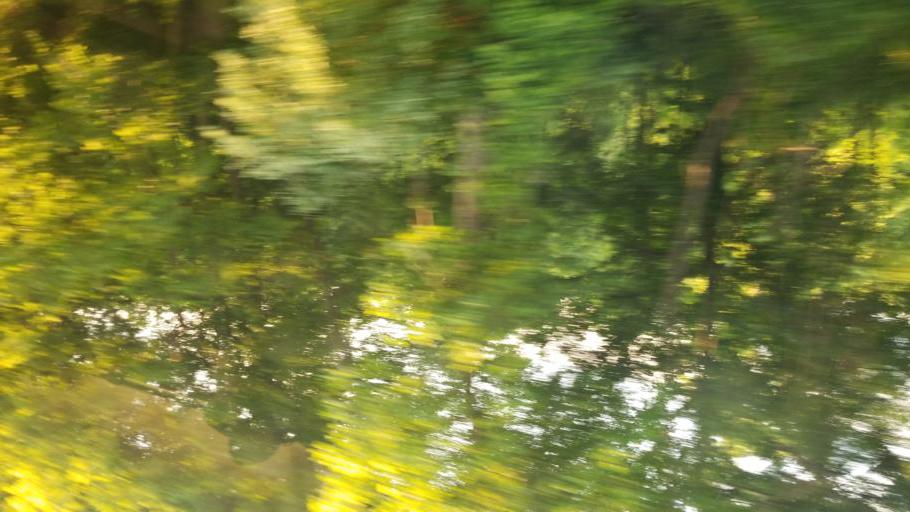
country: US
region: Virginia
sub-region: Prince William County
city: Yorkshire
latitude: 38.7741
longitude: -77.4148
